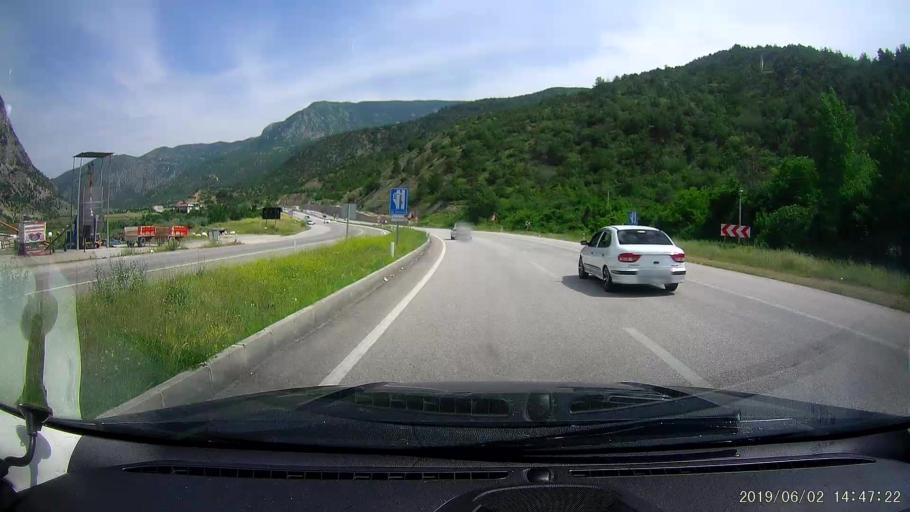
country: TR
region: Corum
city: Hacihamza
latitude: 41.0698
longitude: 34.4587
